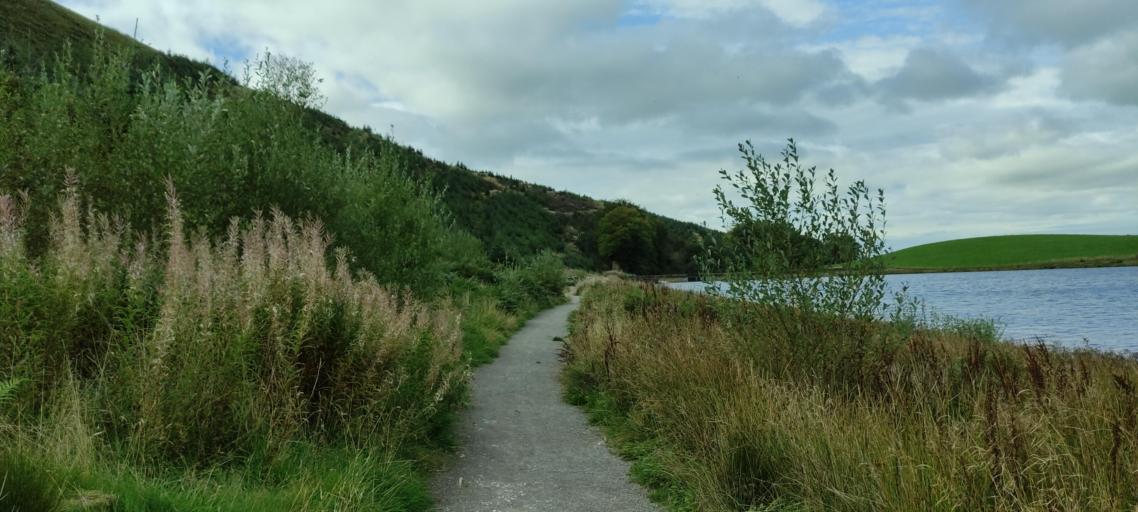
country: GB
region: England
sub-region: Cumbria
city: Frizington
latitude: 54.5620
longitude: -3.4013
